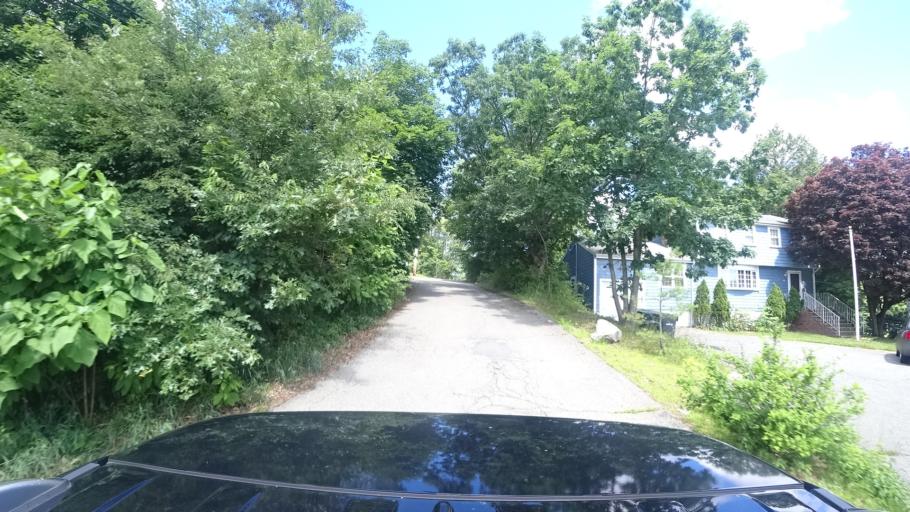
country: US
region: Massachusetts
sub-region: Norfolk County
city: Dedham
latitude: 42.2534
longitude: -71.1555
